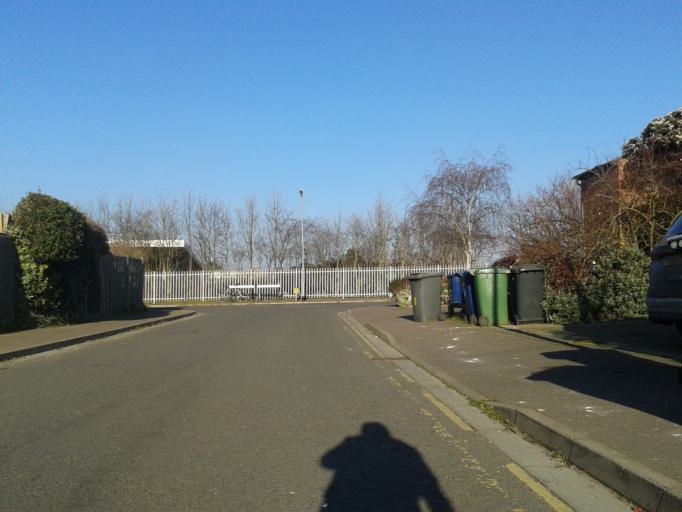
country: GB
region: England
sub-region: Cambridgeshire
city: Cambridge
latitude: 52.2103
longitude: 0.1430
